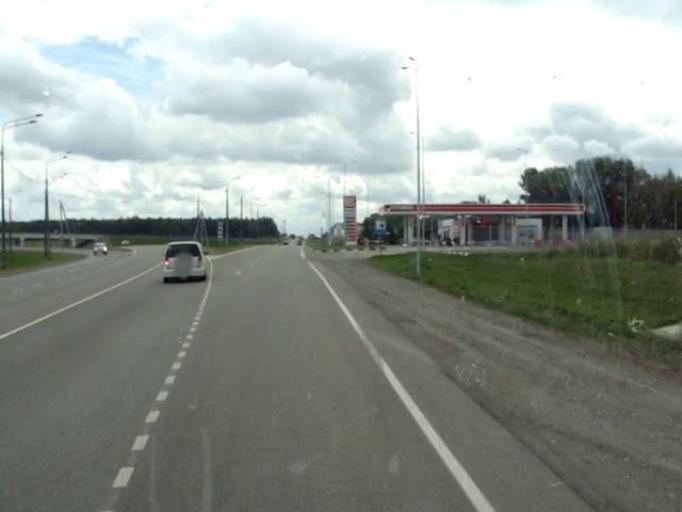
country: RU
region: Altai Krai
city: Zarya
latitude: 52.5805
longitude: 85.1758
